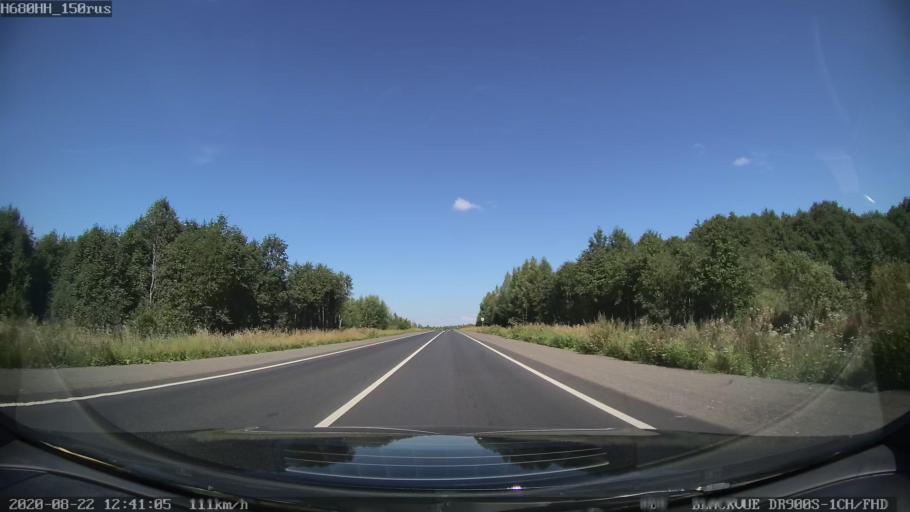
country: RU
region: Tverskaya
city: Rameshki
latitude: 57.3431
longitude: 36.0972
